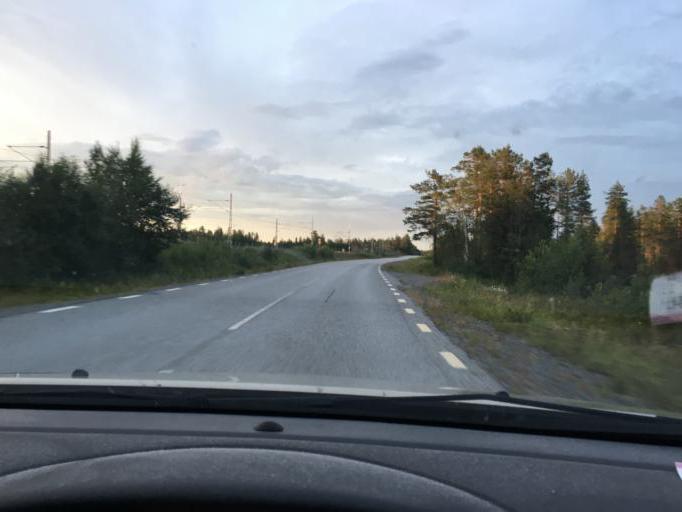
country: SE
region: Norrbotten
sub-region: Lulea Kommun
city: Ranea
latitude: 66.0488
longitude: 22.3529
